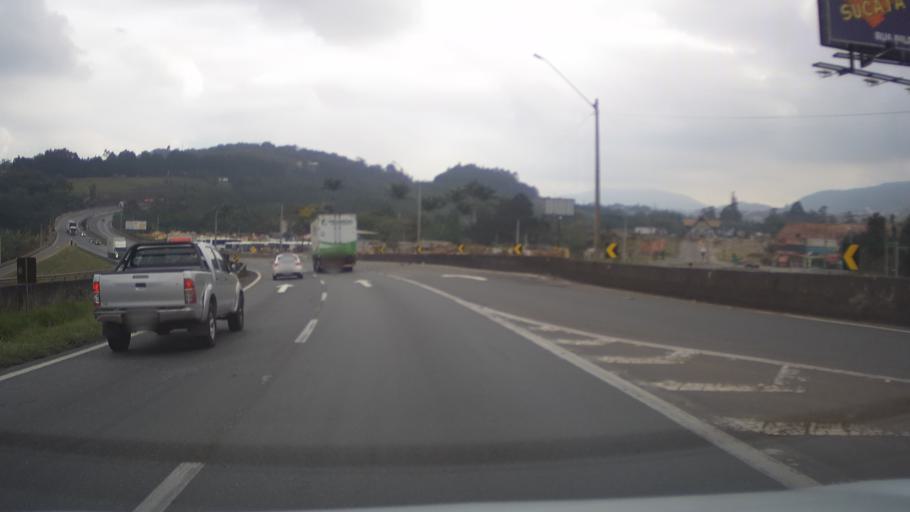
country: BR
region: Minas Gerais
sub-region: Extrema
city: Extrema
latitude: -22.8647
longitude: -46.3458
